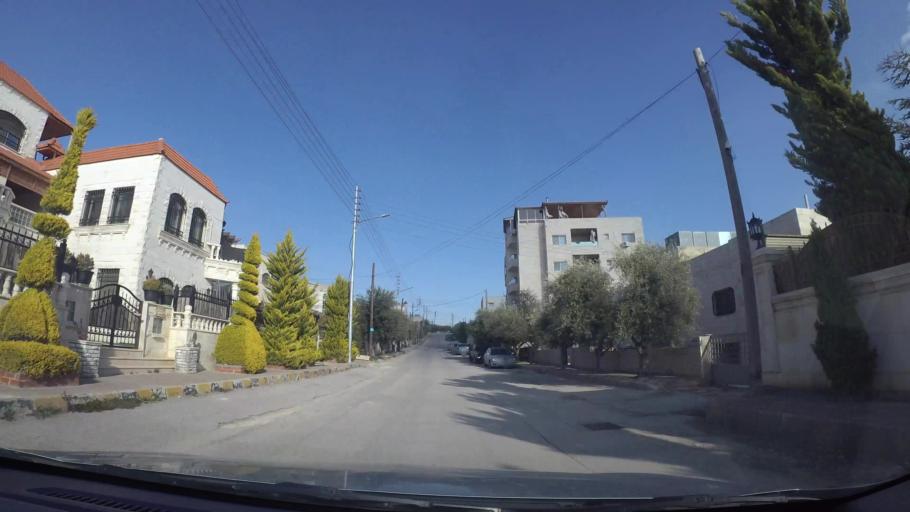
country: JO
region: Amman
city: Al Bunayyat ash Shamaliyah
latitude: 31.8986
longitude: 35.9188
